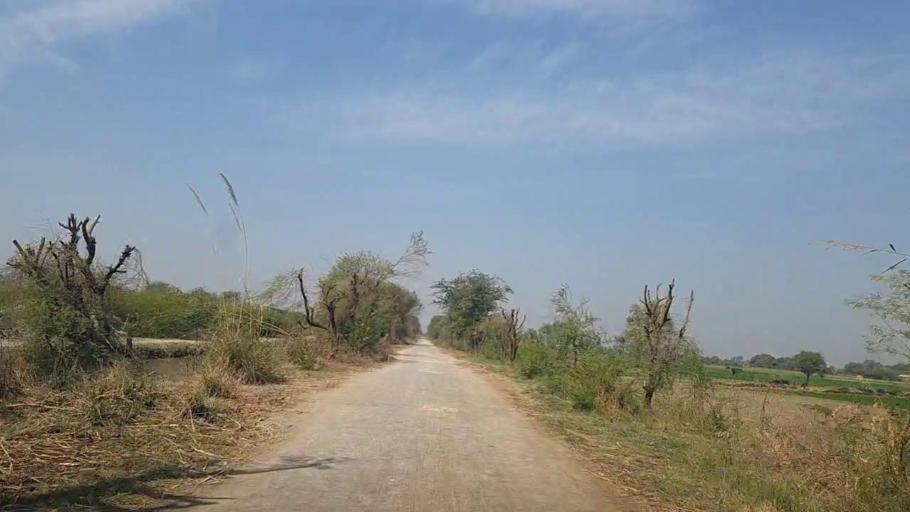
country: PK
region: Sindh
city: Mirpur Khas
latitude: 25.4882
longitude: 68.9231
